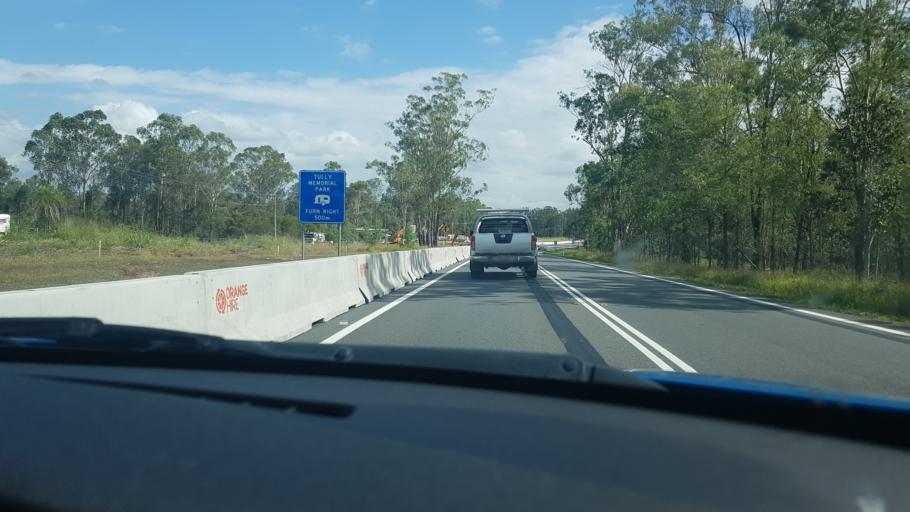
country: AU
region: Queensland
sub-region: Logan
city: North Maclean
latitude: -27.7732
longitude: 153.0147
